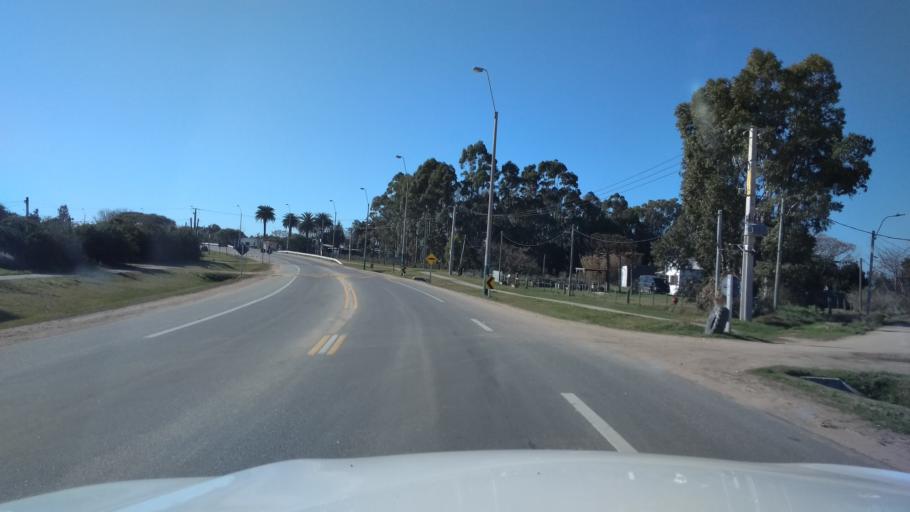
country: UY
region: Canelones
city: Atlantida
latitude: -34.7421
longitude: -55.7656
